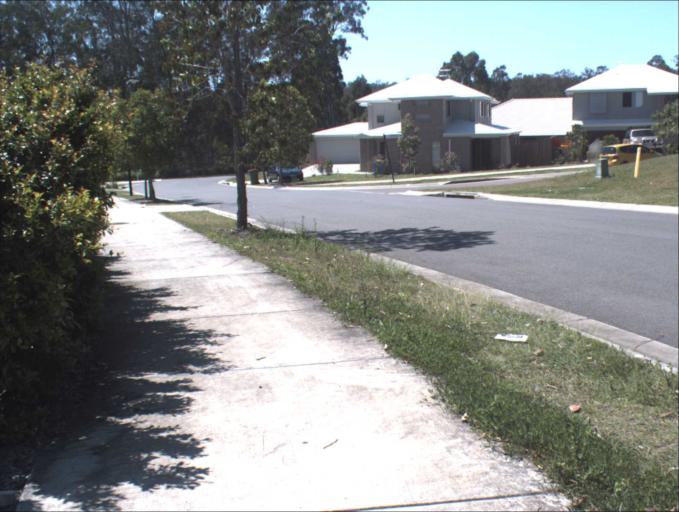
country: AU
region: Queensland
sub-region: Logan
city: Waterford West
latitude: -27.7127
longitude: 153.1440
